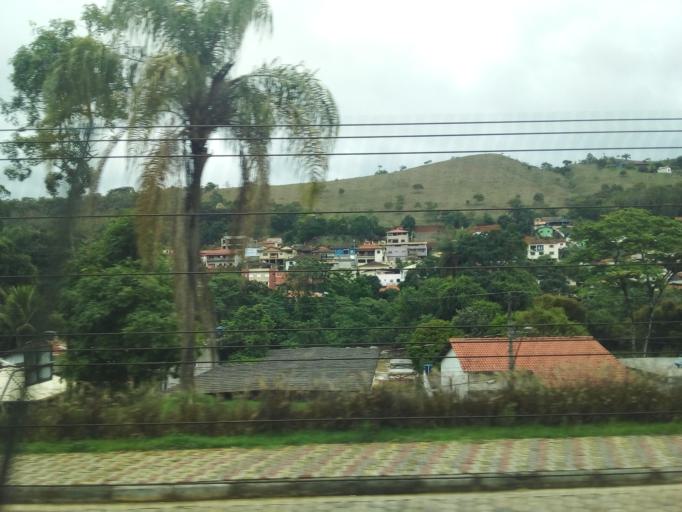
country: BR
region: Minas Gerais
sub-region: Rio Piracicaba
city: Rio Piracicaba
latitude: -19.9330
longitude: -43.1732
